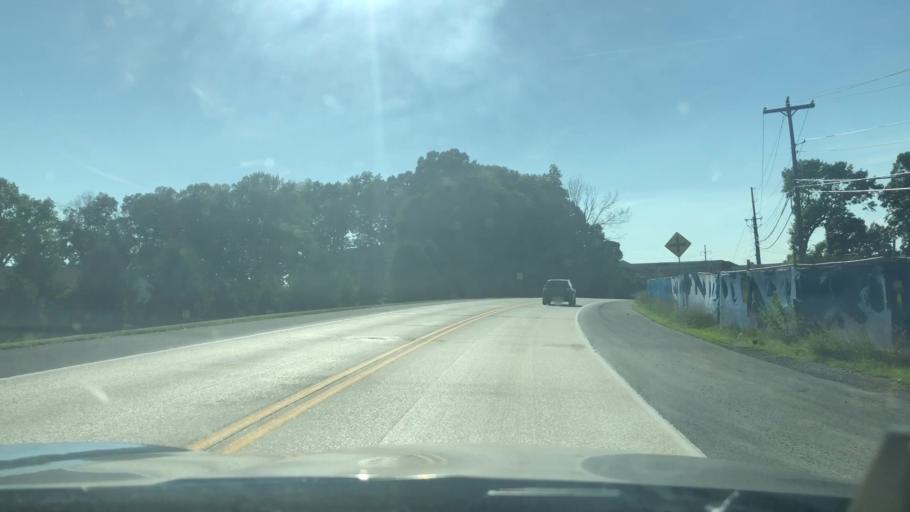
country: US
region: Pennsylvania
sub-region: Cumberland County
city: Shiremanstown
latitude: 40.2102
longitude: -76.9670
